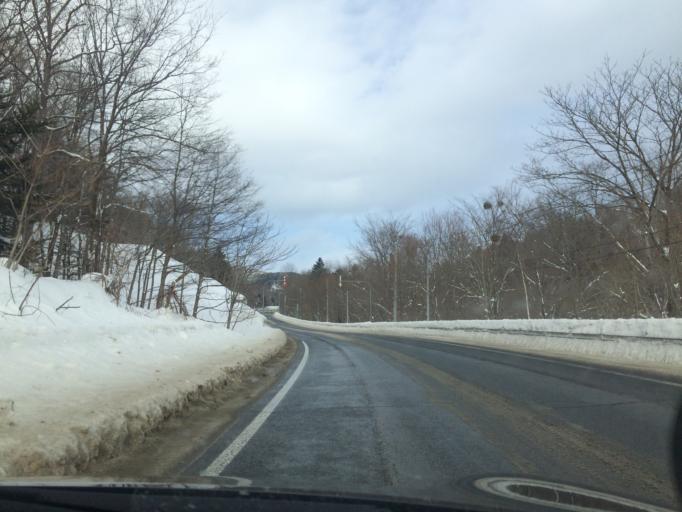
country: JP
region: Hokkaido
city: Shimo-furano
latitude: 42.9686
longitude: 142.3774
